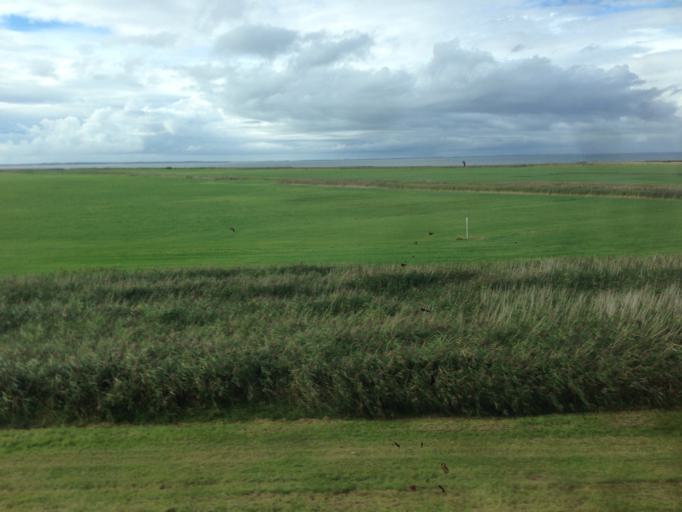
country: DE
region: Schleswig-Holstein
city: Sylt-Ost
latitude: 54.8732
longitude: 8.4803
